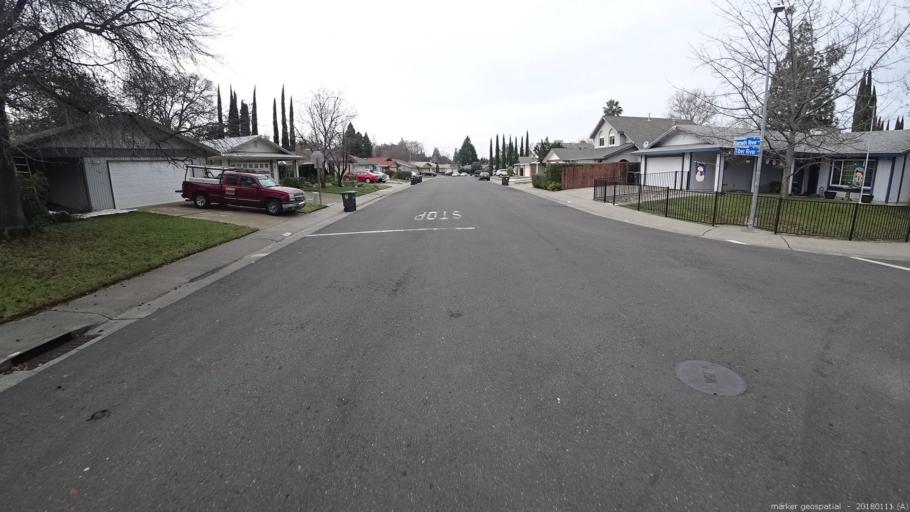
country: US
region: California
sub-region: Sacramento County
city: Fair Oaks
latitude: 38.6183
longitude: -121.2730
